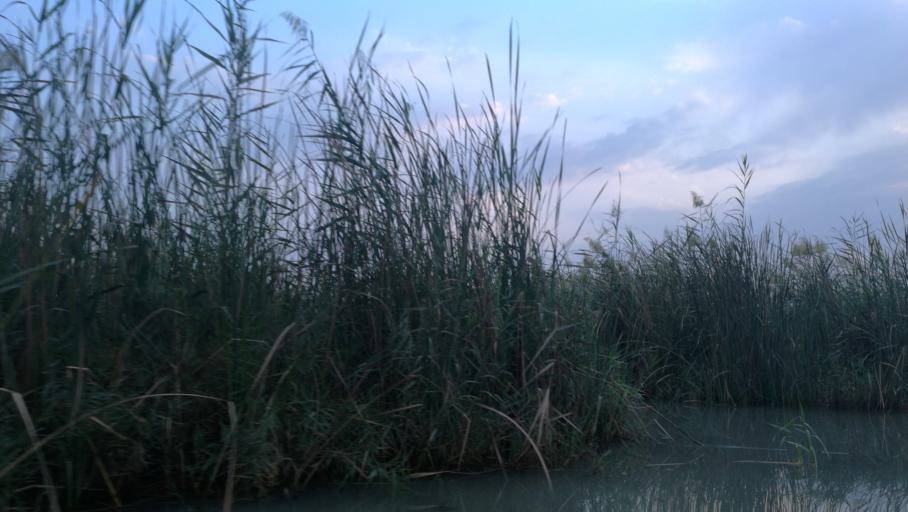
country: IQ
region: Dhi Qar
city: Al Jabayish
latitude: 30.9869
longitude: 47.0427
